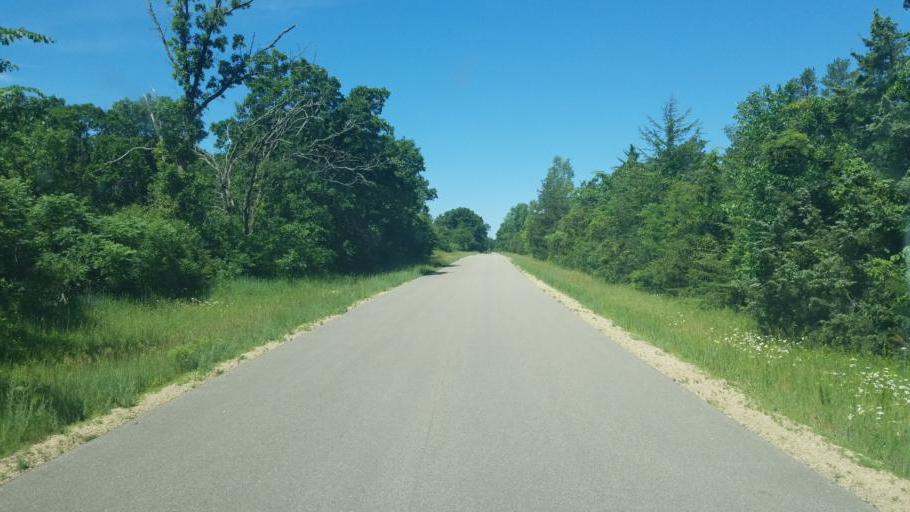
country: US
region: Wisconsin
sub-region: Adams County
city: Adams
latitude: 43.8695
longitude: -89.9387
